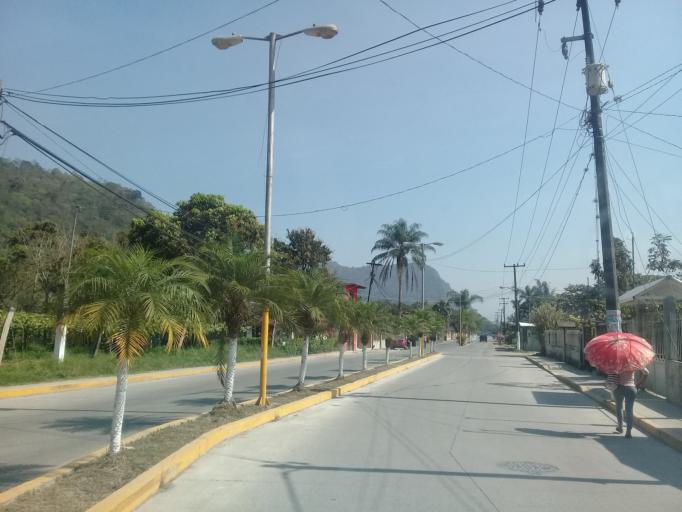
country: MX
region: Veracruz
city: Rafael Delgado
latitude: 18.7856
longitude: -97.0117
